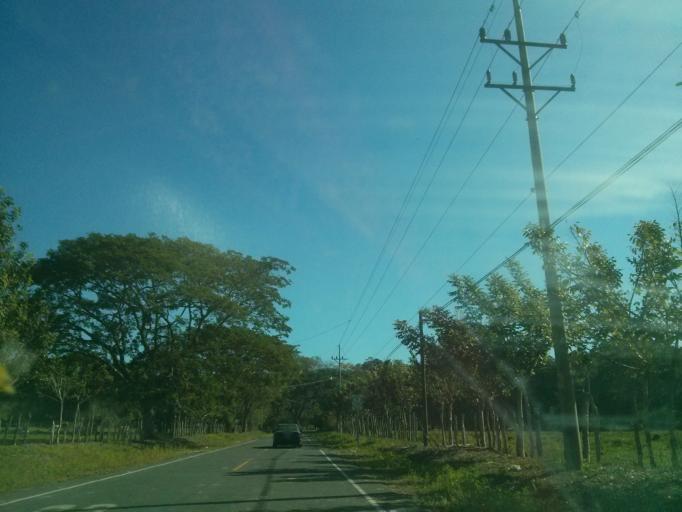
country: CR
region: Puntarenas
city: Paquera
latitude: 9.7553
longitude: -85.0012
